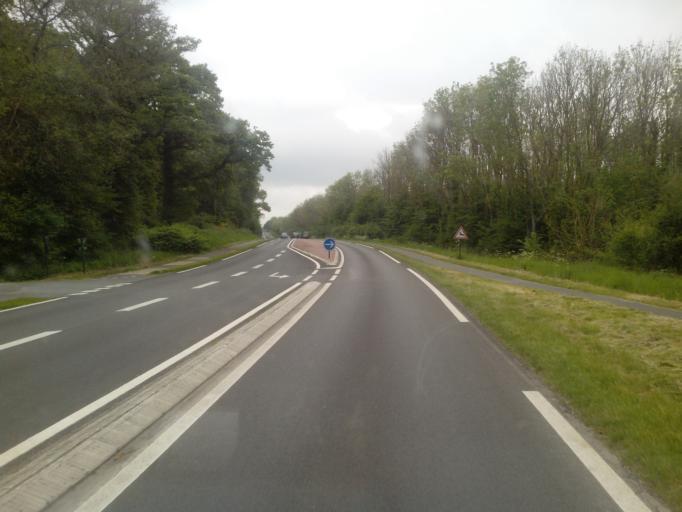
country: FR
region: Nord-Pas-de-Calais
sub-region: Departement du Pas-de-Calais
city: Neufchatel-Hardelot
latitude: 50.6332
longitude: 1.6450
